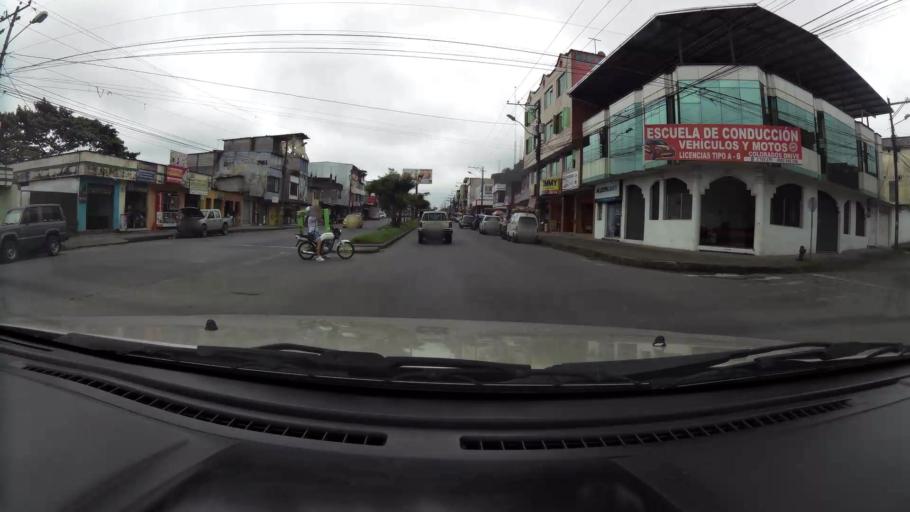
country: EC
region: Santo Domingo de los Tsachilas
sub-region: Canton Santo Domingo de los Colorados
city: Santo Domingo de los Colorados
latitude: -0.2431
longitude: -79.1718
